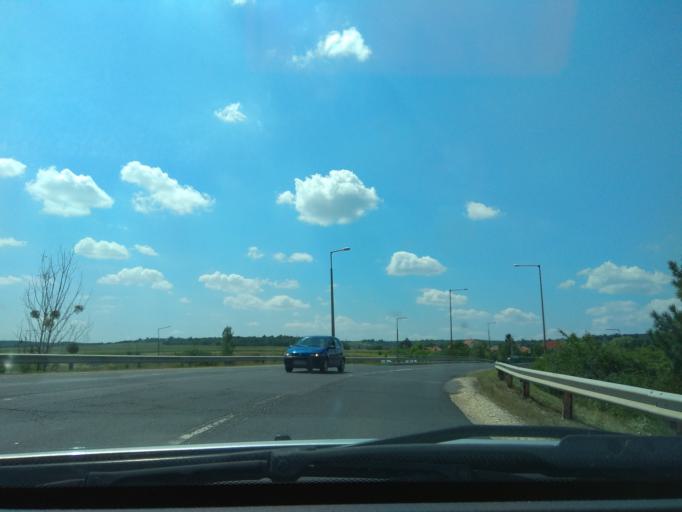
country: HU
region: Borsod-Abauj-Zemplen
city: Malyi
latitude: 48.0529
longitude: 20.7996
